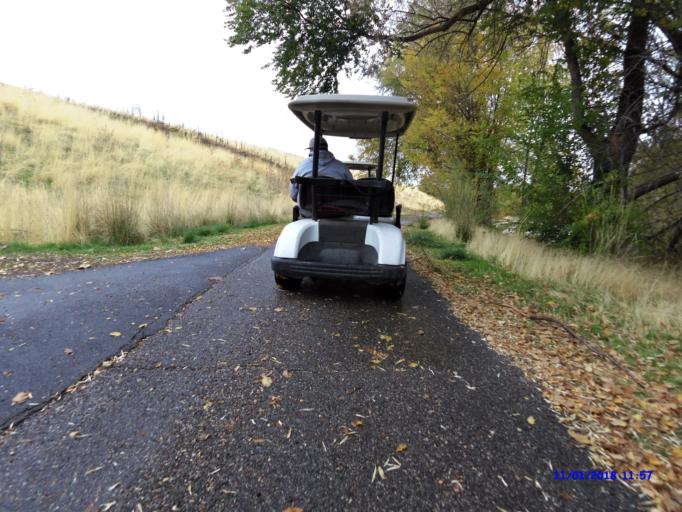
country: US
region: Utah
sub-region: Weber County
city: Ogden
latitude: 41.2340
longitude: -111.9959
